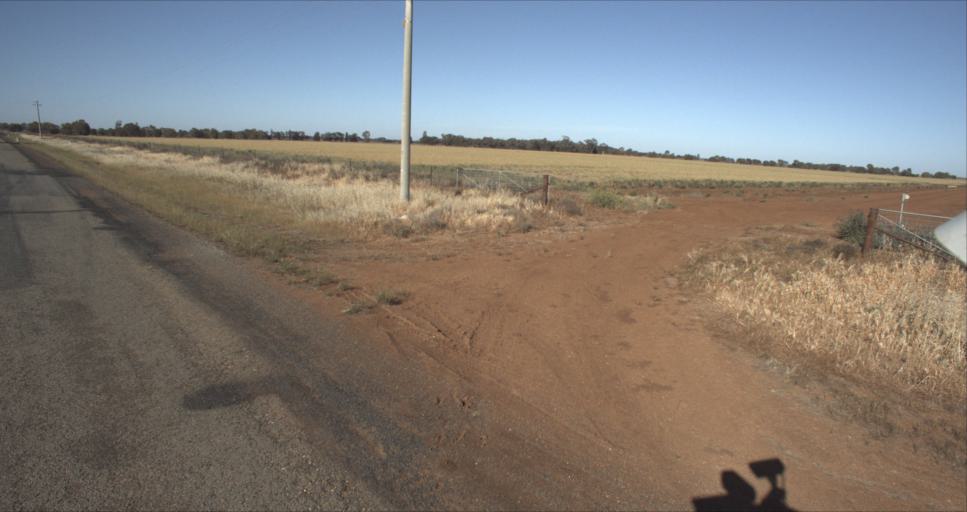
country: AU
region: New South Wales
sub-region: Leeton
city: Leeton
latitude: -34.5601
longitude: 146.2656
